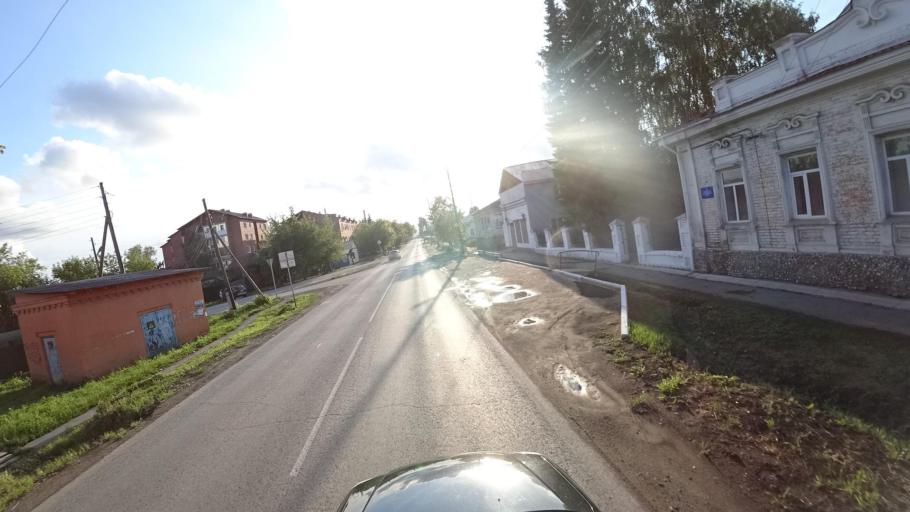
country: RU
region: Sverdlovsk
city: Kamyshlov
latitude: 56.8470
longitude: 62.7088
